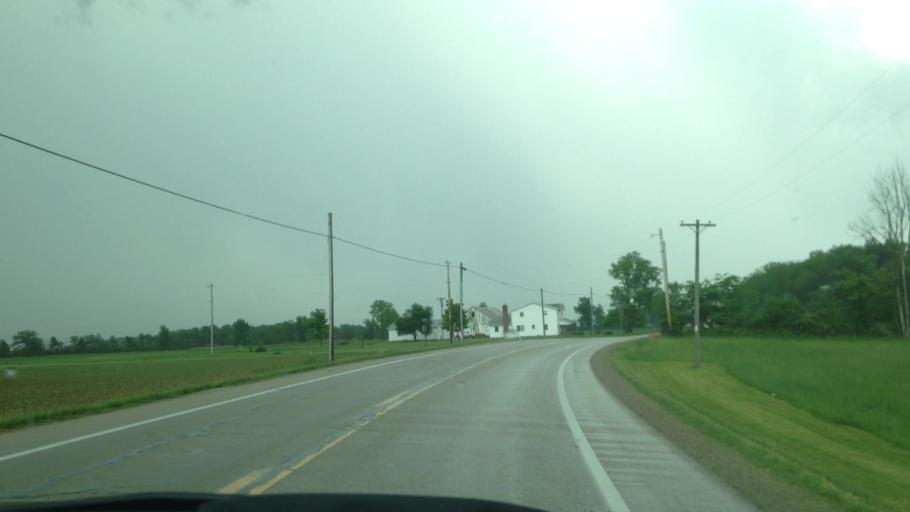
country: US
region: Ohio
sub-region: Darke County
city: Greenville
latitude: 40.1513
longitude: -84.6644
